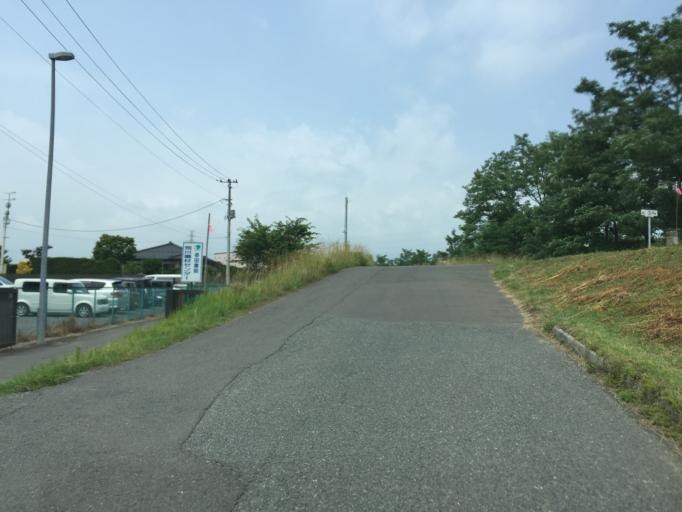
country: JP
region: Fukushima
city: Fukushima-shi
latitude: 37.7532
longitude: 140.4318
